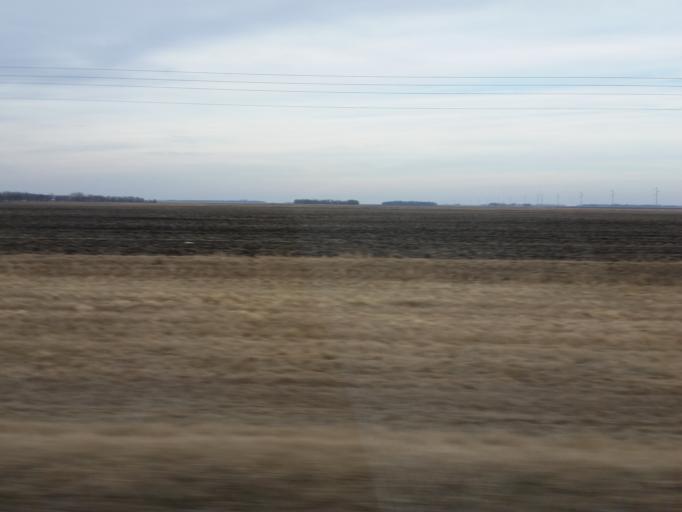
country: US
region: North Dakota
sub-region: Cass County
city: Casselton
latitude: 47.0672
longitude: -97.2180
